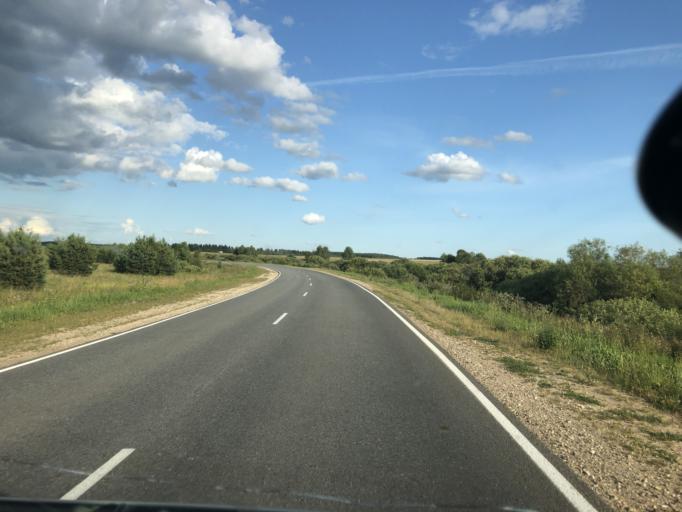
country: RU
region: Kaluga
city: Yukhnov
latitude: 54.7016
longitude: 35.2715
